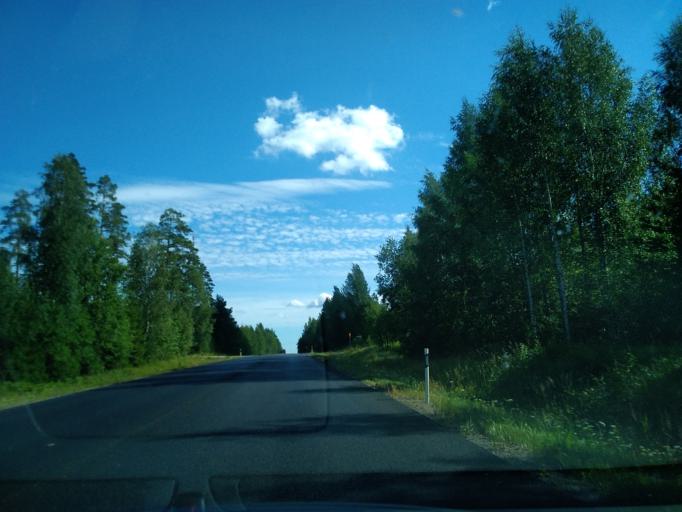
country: FI
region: Haeme
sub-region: Haemeenlinna
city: Renko
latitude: 60.9347
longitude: 24.3687
